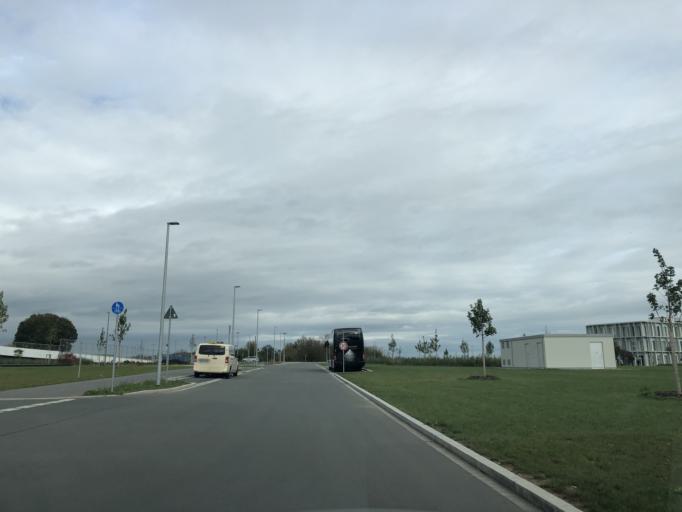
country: DE
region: Bavaria
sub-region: Regierungsbezirk Mittelfranken
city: Herzogenaurach
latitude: 49.5787
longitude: 10.9184
